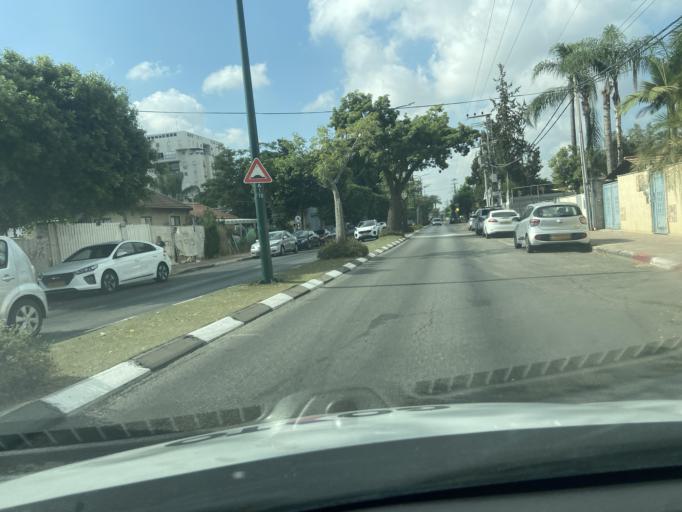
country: IL
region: Central District
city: Yehud
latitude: 32.0357
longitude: 34.8859
